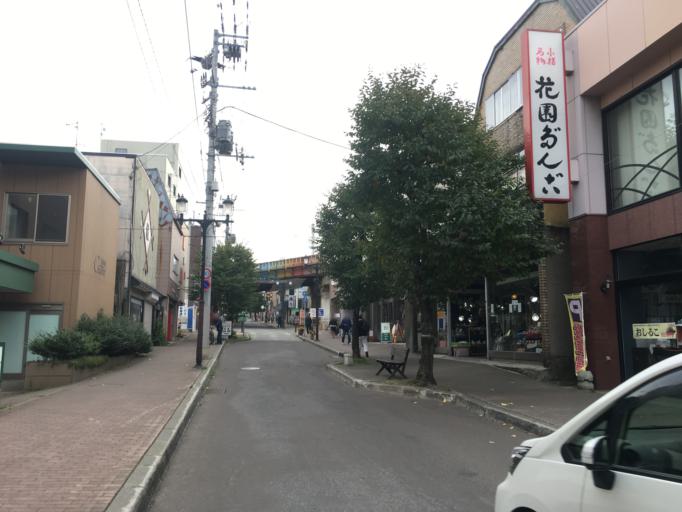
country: JP
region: Hokkaido
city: Otaru
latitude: 43.1938
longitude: 140.9994
